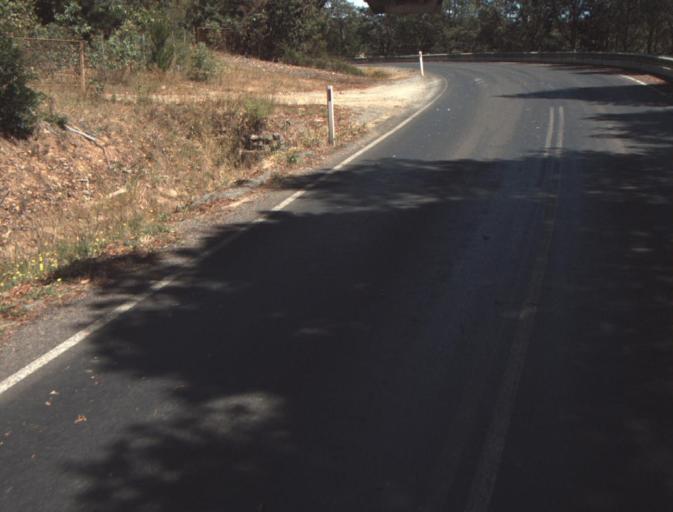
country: AU
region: Tasmania
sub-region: Launceston
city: Newstead
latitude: -41.3244
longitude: 147.3591
